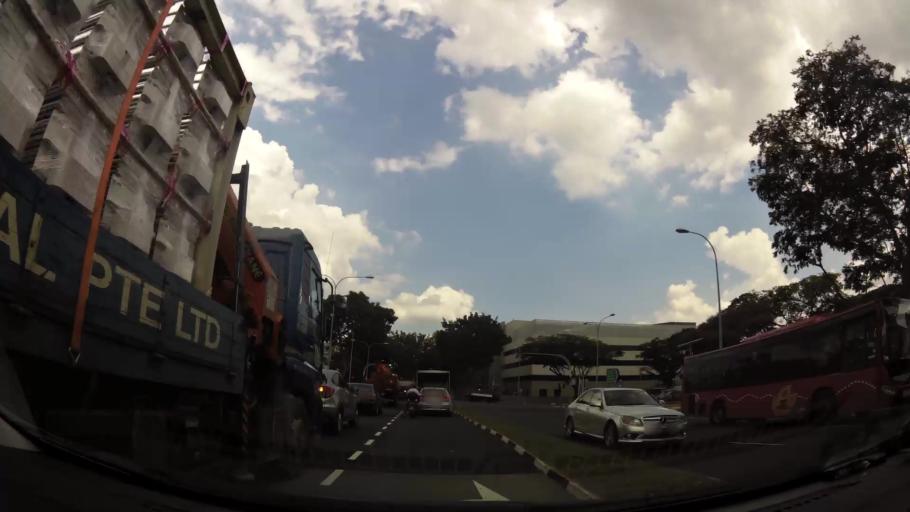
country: MY
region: Johor
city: Johor Bahru
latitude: 1.4501
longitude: 103.8024
